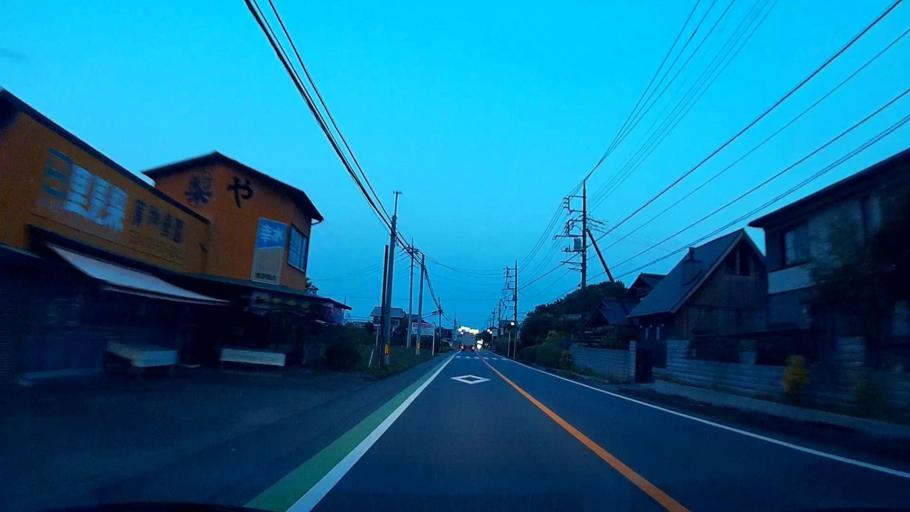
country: JP
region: Gunma
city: Annaka
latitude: 36.3674
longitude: 138.9086
